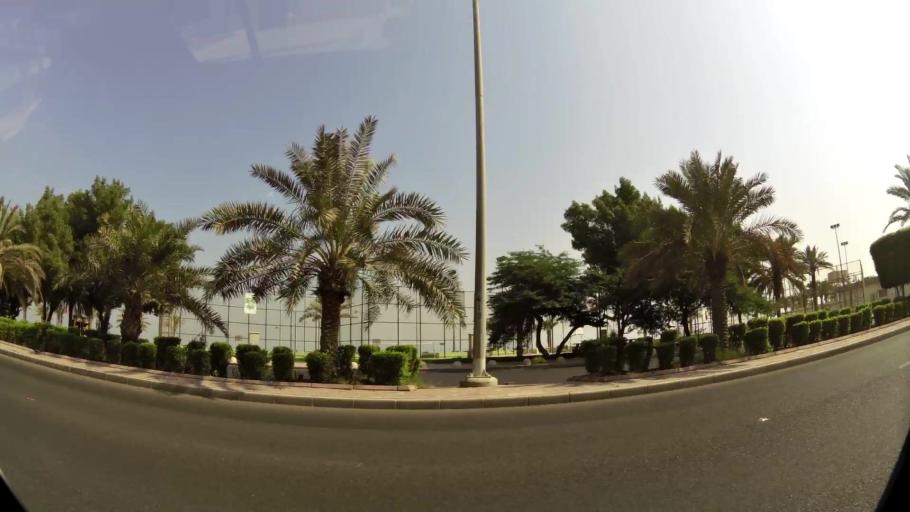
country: KW
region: Al Ahmadi
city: Al Fintas
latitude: 29.1762
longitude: 48.1222
